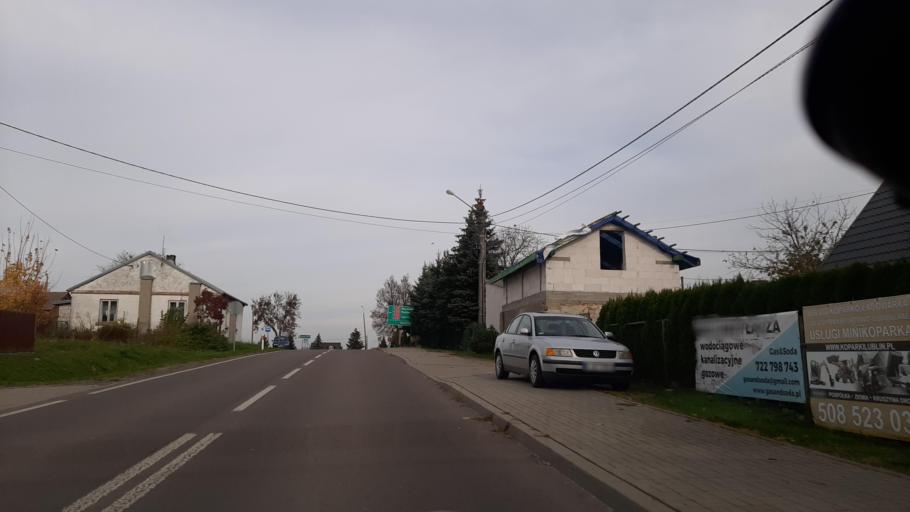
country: PL
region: Lublin Voivodeship
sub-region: Powiat pulawski
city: Markuszow
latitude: 51.3679
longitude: 22.2804
